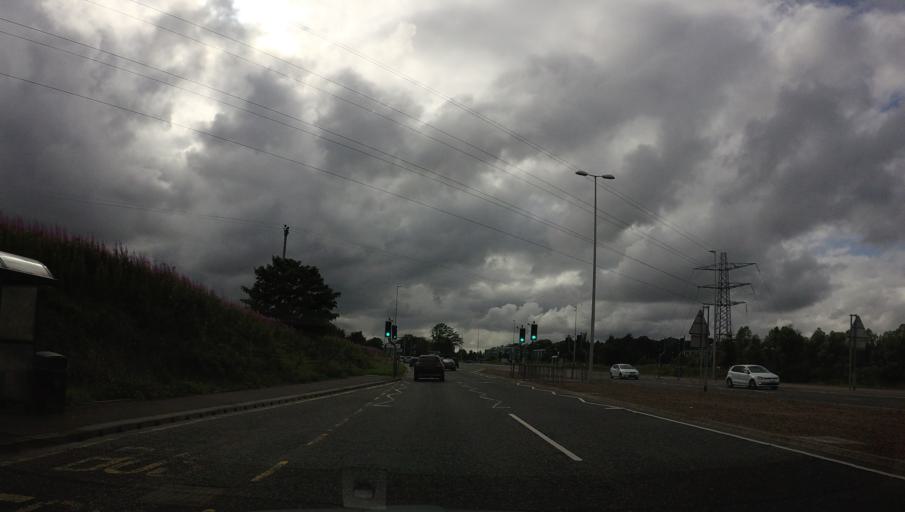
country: GB
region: Scotland
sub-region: Aberdeenshire
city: Westhill
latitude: 57.1467
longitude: -2.2218
